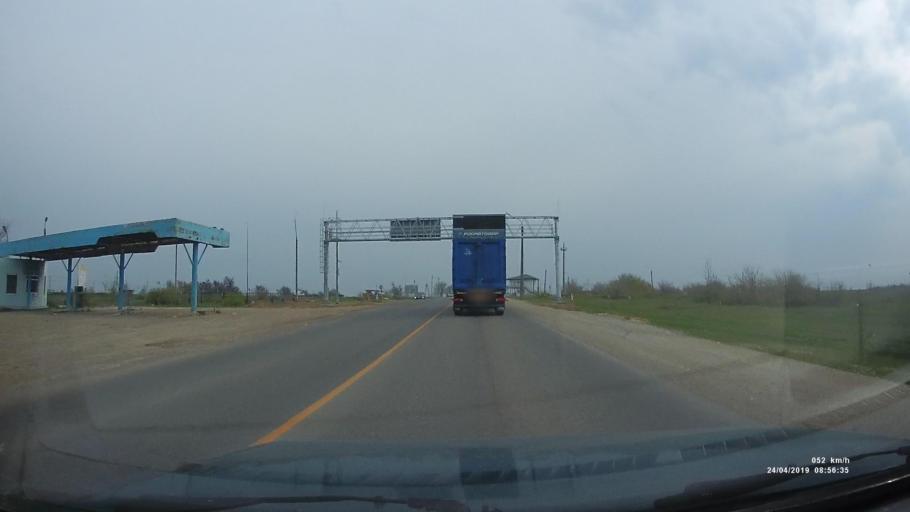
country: RU
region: Kalmykiya
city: Arshan'
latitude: 46.3019
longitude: 44.1862
